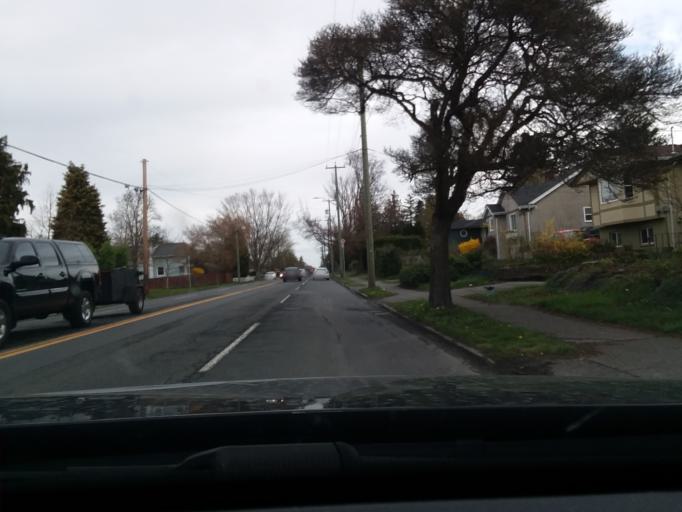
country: CA
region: British Columbia
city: Oak Bay
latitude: 48.4515
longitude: -123.3331
